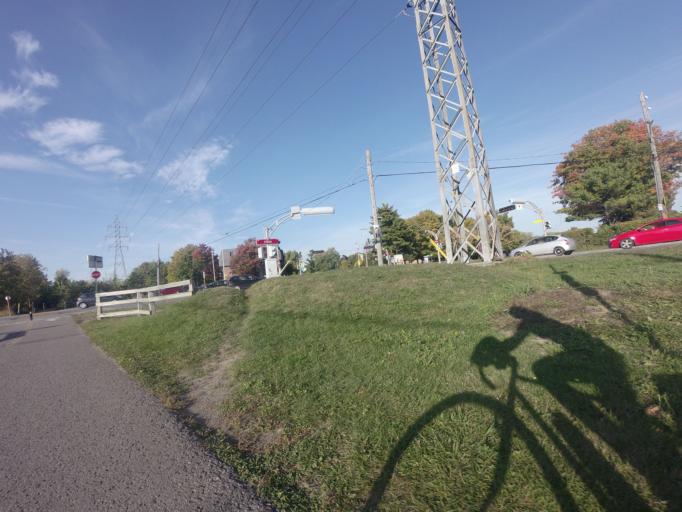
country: CA
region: Quebec
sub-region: Laurentides
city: Saint-Jerome
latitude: 45.7873
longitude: -73.9967
